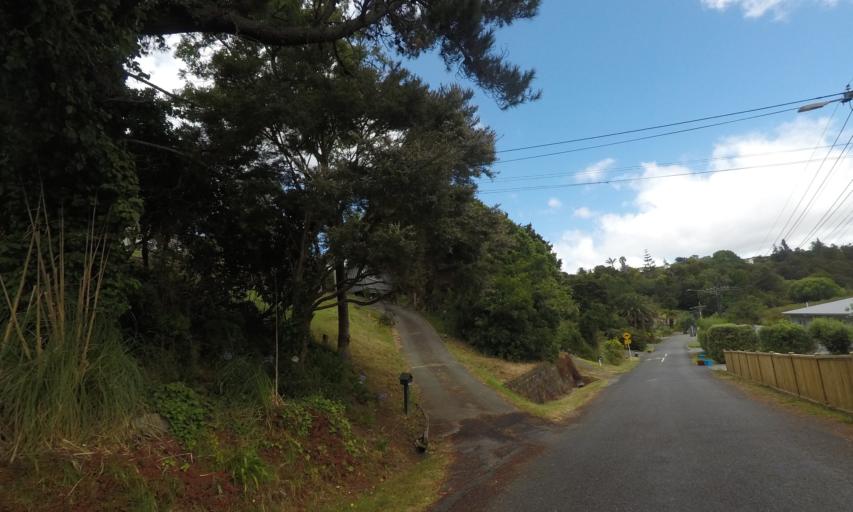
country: NZ
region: Northland
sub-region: Whangarei
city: Whangarei
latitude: -35.7439
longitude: 174.3603
